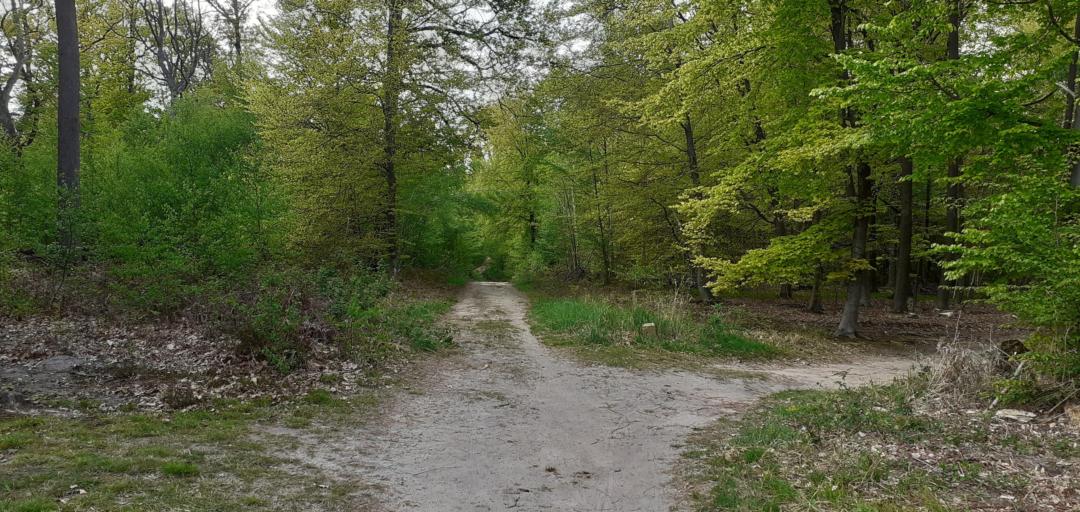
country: FR
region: Picardie
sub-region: Departement de l'Oise
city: Orry-la-Ville
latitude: 49.1201
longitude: 2.5071
